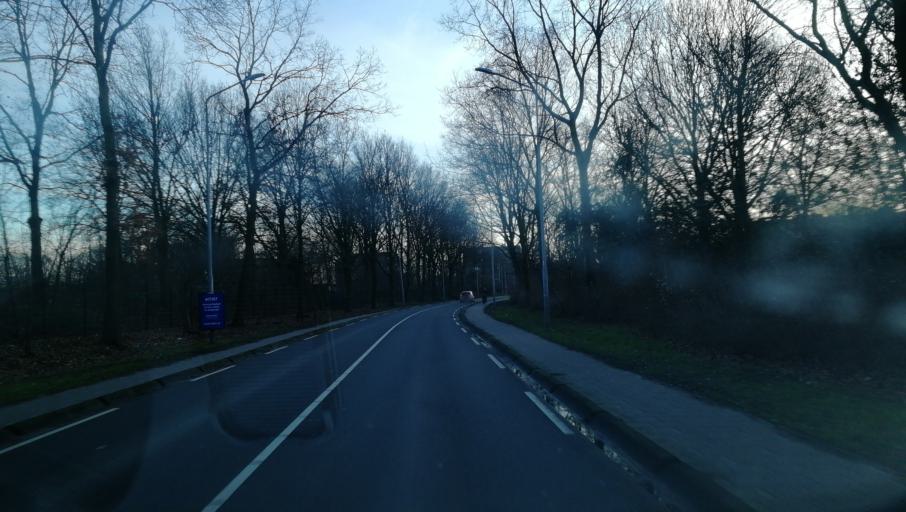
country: NL
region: Limburg
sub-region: Gemeente Venlo
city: Tegelen
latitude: 51.3671
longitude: 6.1357
